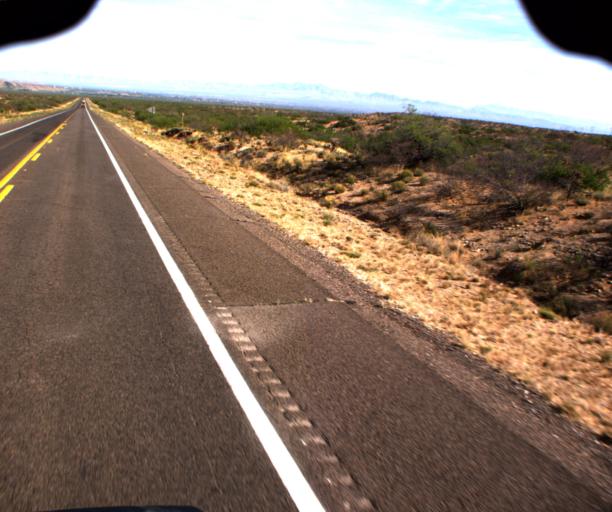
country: US
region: Arizona
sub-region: Graham County
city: Swift Trail Junction
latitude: 32.6296
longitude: -109.6910
